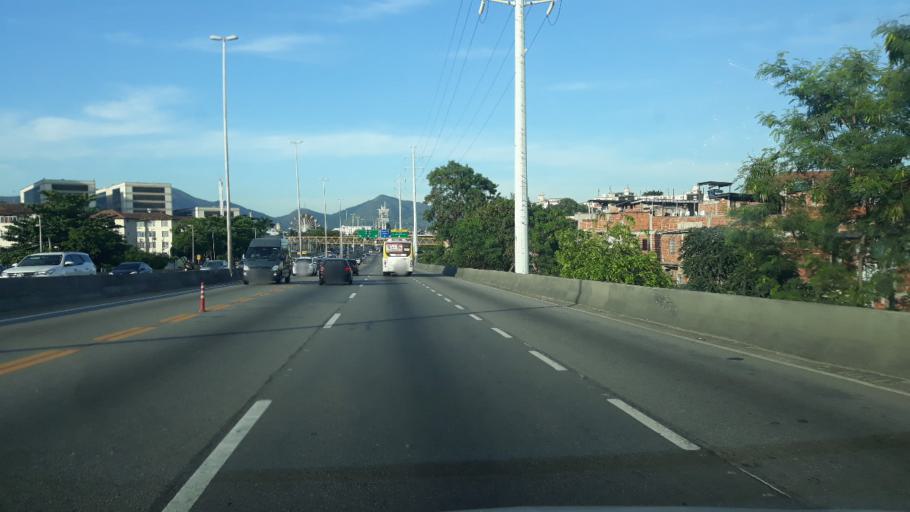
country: BR
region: Rio de Janeiro
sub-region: Rio De Janeiro
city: Rio de Janeiro
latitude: -22.8736
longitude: -43.2687
